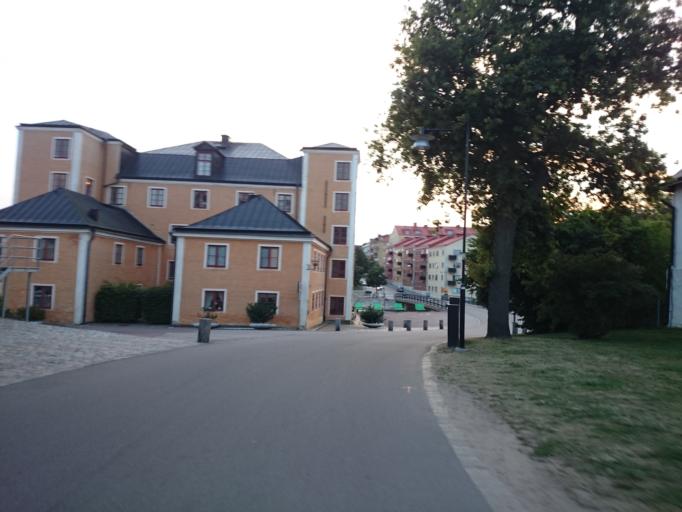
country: SE
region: Blekinge
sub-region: Karlskrona Kommun
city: Karlskrona
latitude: 56.1607
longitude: 15.5973
